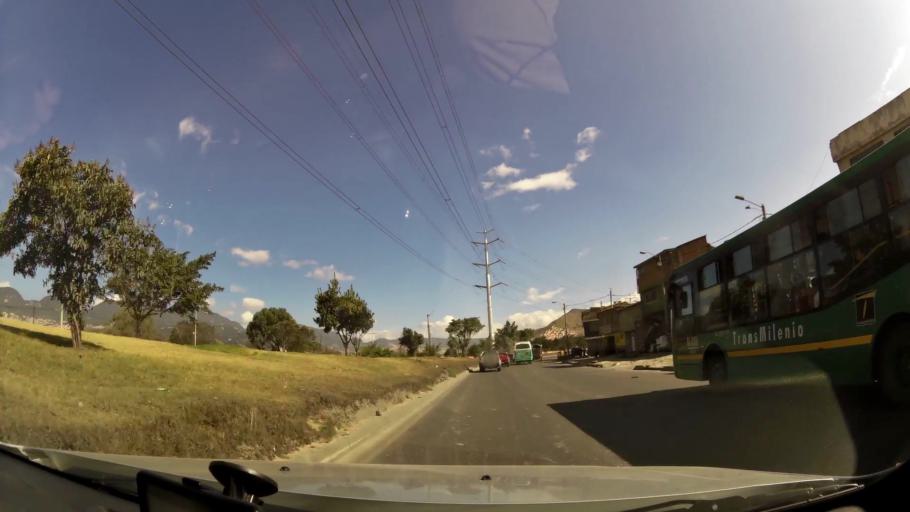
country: CO
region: Bogota D.C.
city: Bogota
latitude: 4.5522
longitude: -74.1368
